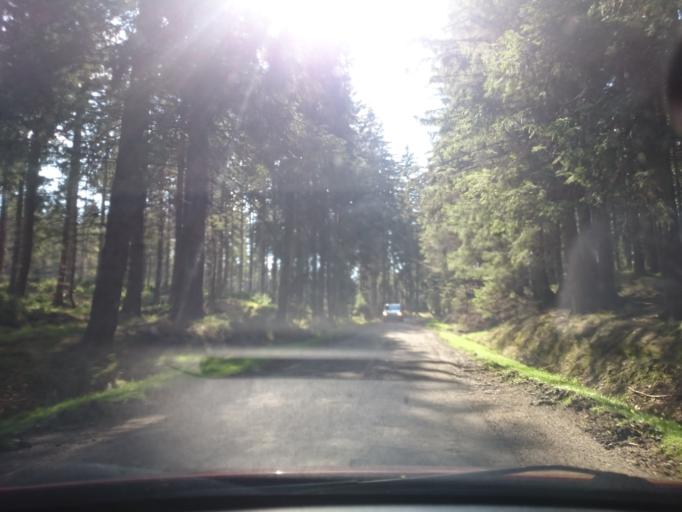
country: PL
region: Lower Silesian Voivodeship
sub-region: Powiat klodzki
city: Polanica-Zdroj
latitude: 50.2996
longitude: 16.4909
